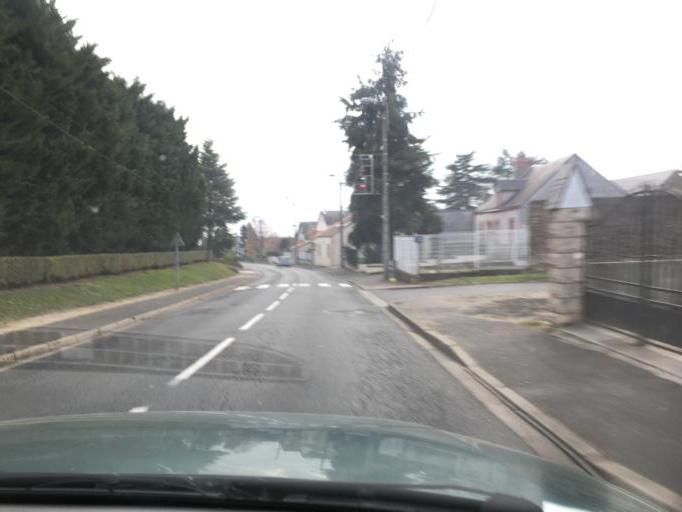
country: FR
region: Centre
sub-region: Departement du Loiret
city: Saran
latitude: 47.9545
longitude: 1.8788
